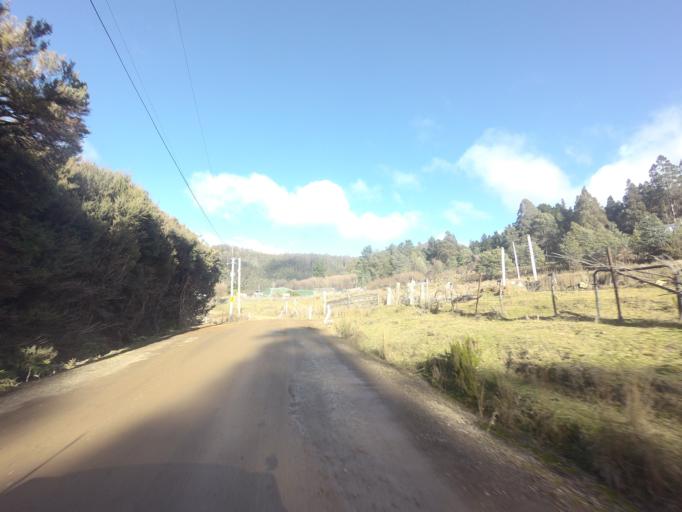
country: AU
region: Tasmania
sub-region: Glenorchy
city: Berriedale
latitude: -42.8550
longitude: 147.1672
